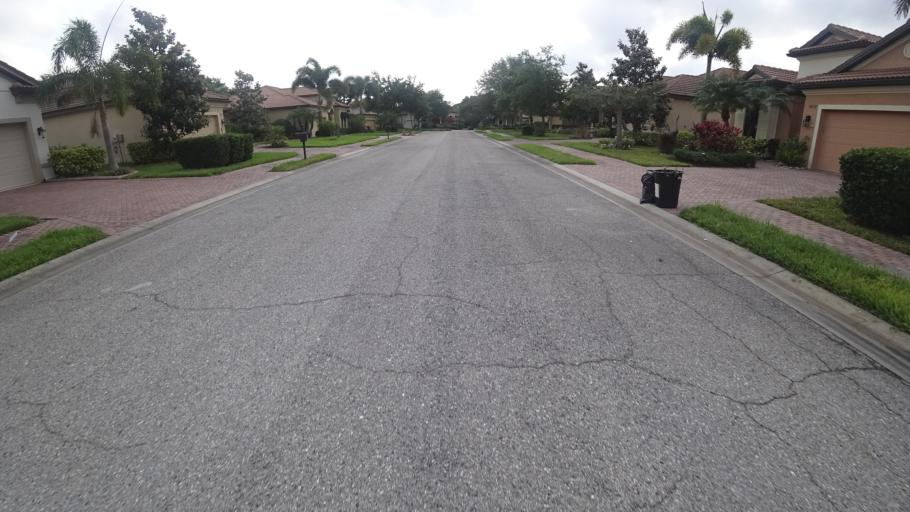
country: US
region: Florida
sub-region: Sarasota County
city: North Sarasota
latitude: 27.3975
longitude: -82.5171
